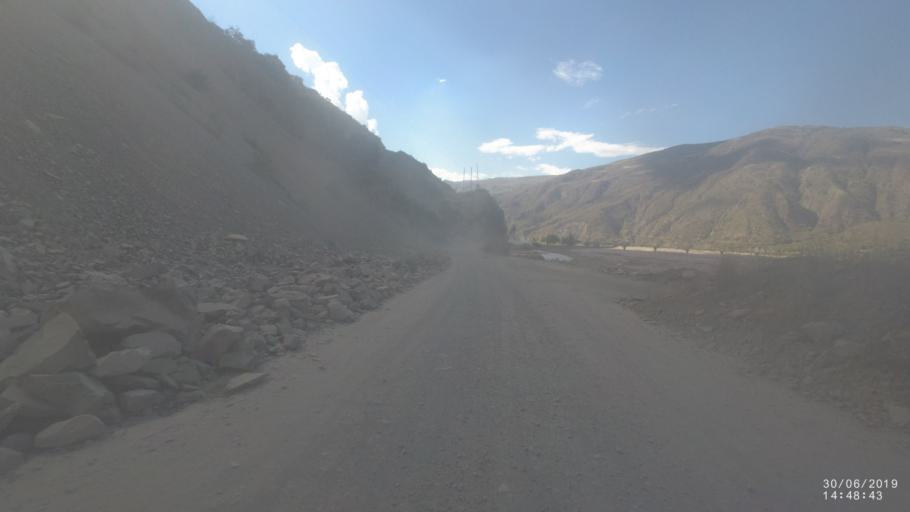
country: BO
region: Cochabamba
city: Irpa Irpa
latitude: -17.7875
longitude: -66.3423
